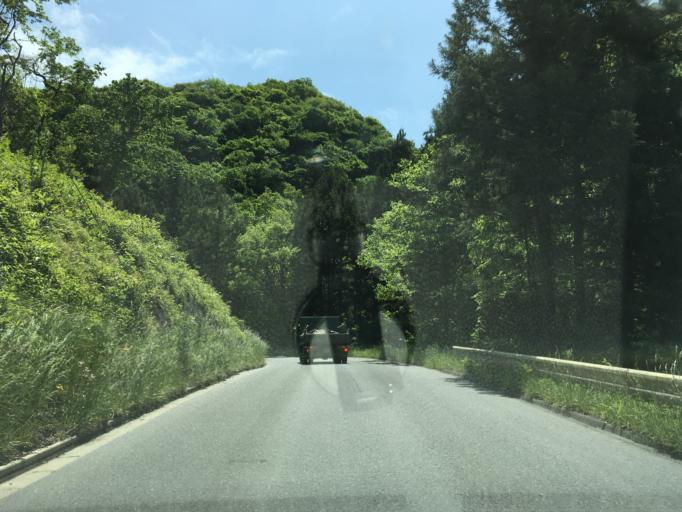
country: JP
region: Miyagi
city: Wakuya
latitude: 38.6567
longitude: 141.3186
